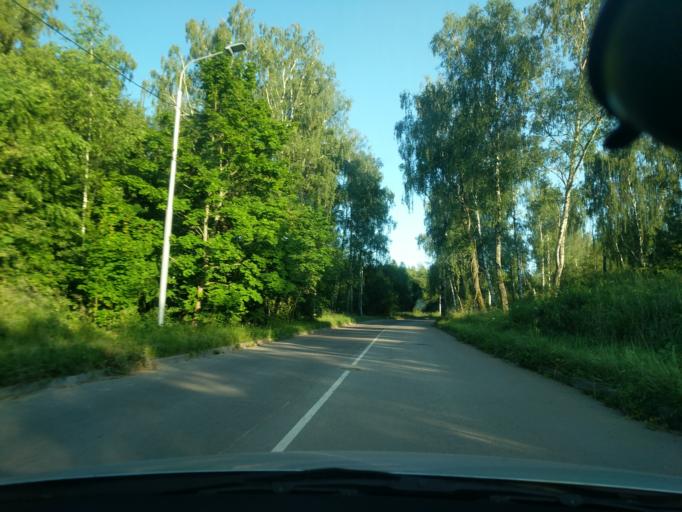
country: RU
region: Moskovskaya
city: Pushchino
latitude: 54.8422
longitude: 37.6414
